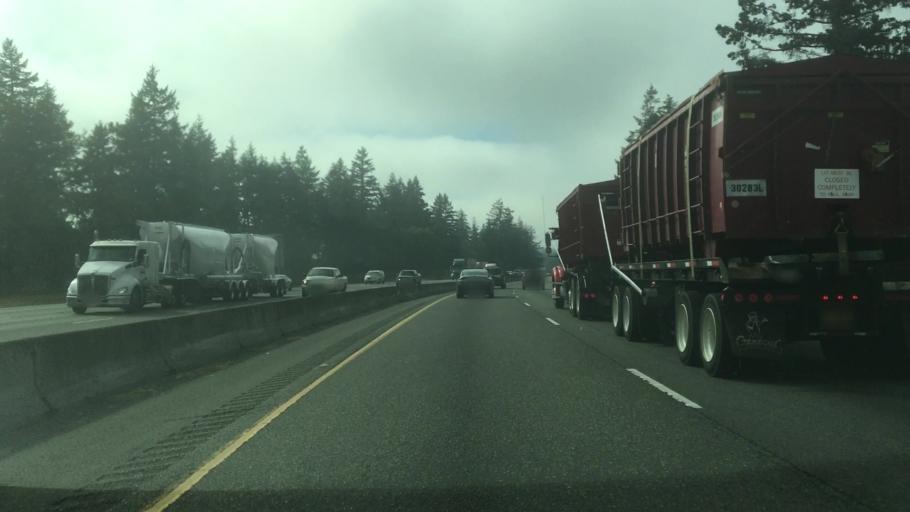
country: US
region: Washington
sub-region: Pierce County
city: Fort Lewis
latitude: 47.1105
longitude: -122.5713
